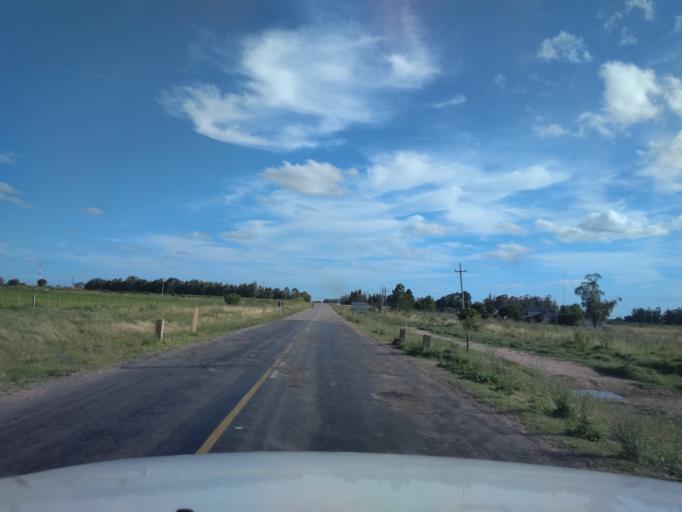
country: UY
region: Canelones
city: San Ramon
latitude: -34.2354
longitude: -55.9273
